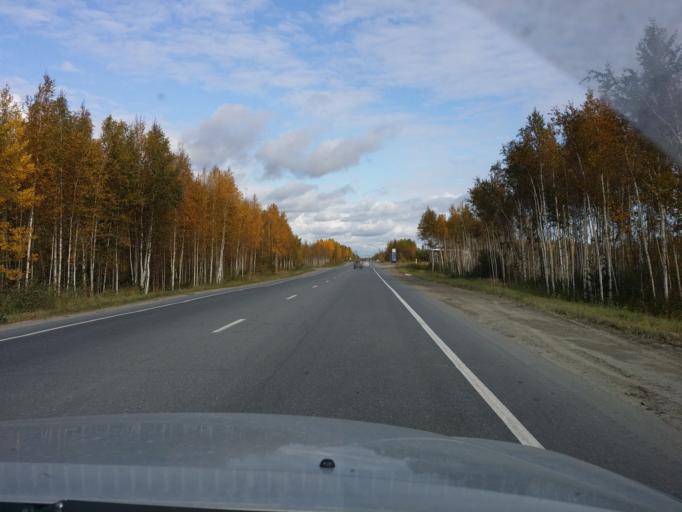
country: RU
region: Khanty-Mansiyskiy Avtonomnyy Okrug
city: Megion
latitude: 61.0675
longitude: 76.1157
